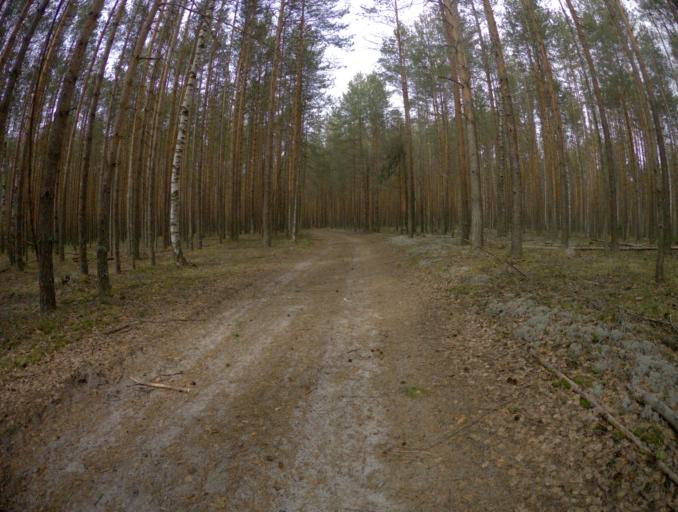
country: RU
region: Vladimir
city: Raduzhnyy
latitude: 55.9471
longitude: 40.2728
